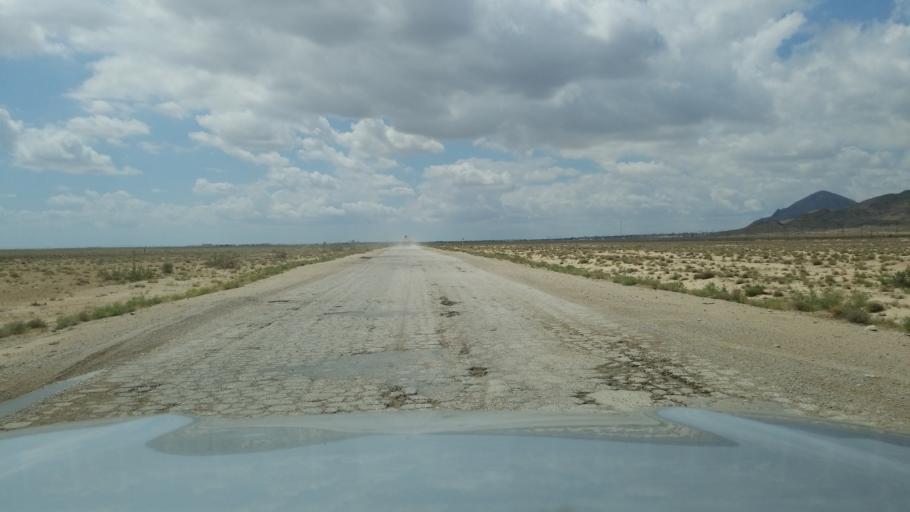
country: TM
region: Balkan
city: Balkanabat
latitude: 39.4823
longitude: 54.4427
